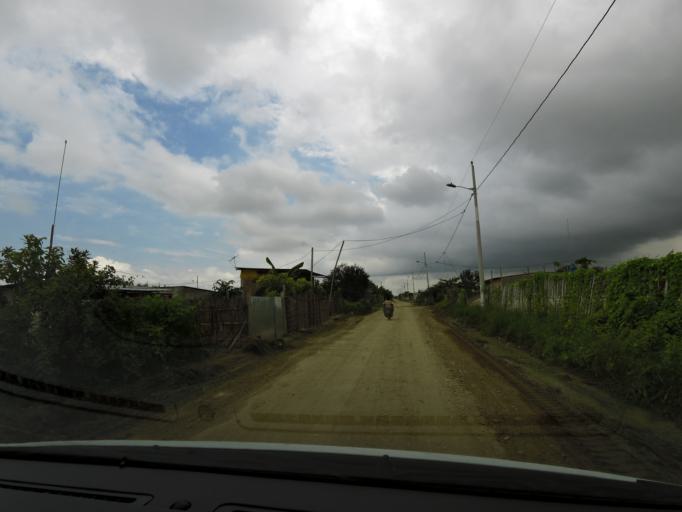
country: EC
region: El Oro
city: Huaquillas
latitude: -3.4861
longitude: -80.2065
